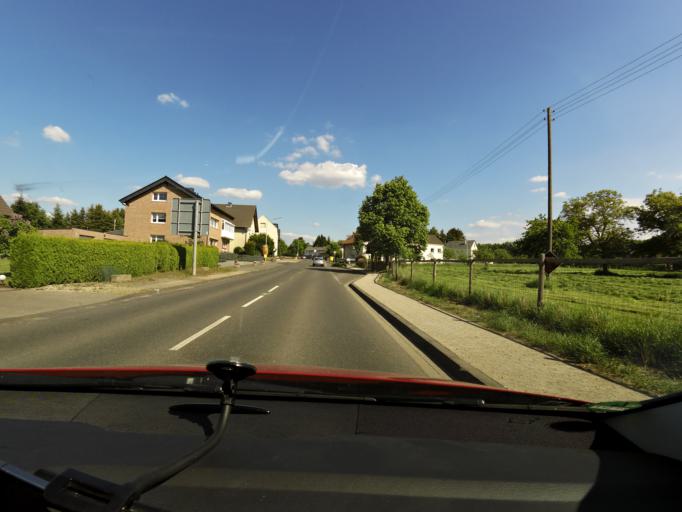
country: DE
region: Rheinland-Pfalz
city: Dernau
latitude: 50.5737
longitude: 7.0595
